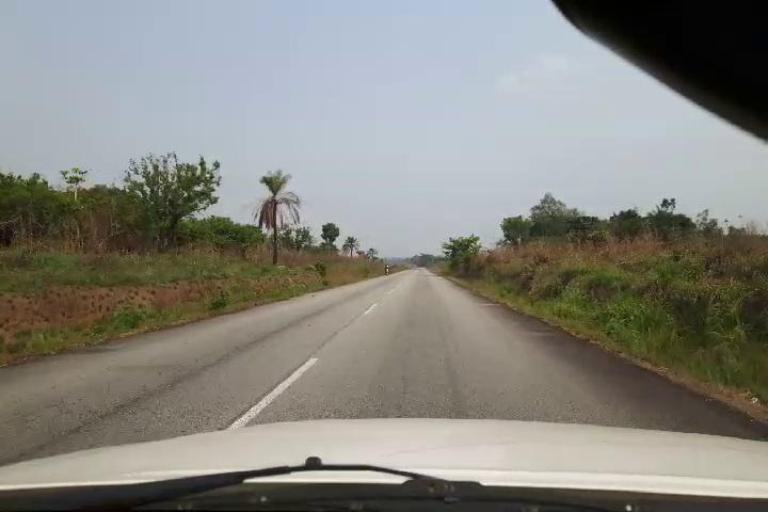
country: SL
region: Southern Province
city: Baiima
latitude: 8.1505
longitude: -11.9100
